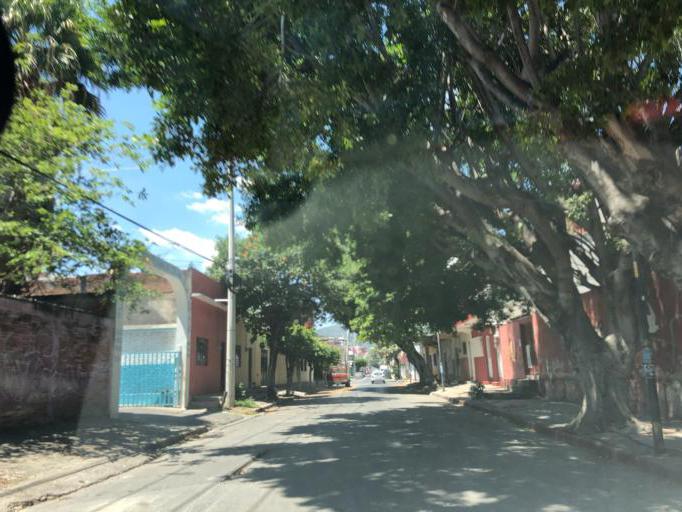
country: MX
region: Chiapas
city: Tuxtla Gutierrez
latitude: 16.7583
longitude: -93.1197
